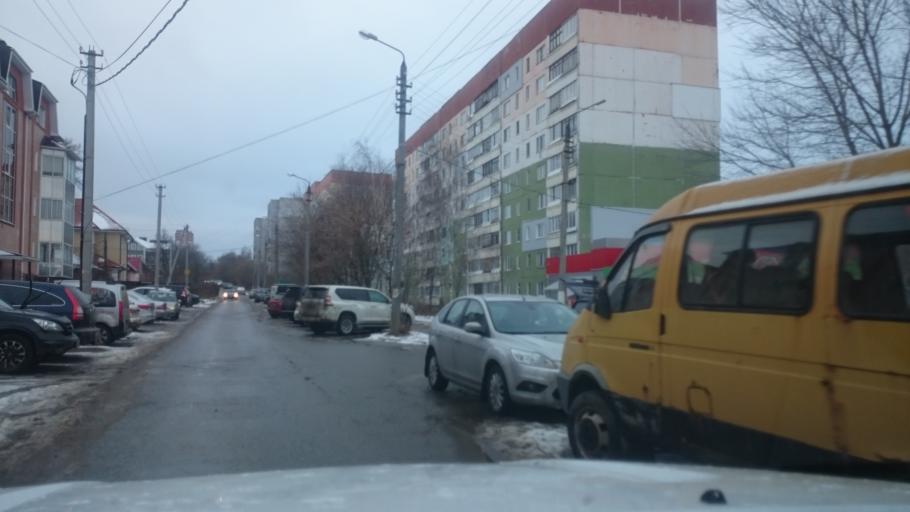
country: RU
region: Tula
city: Tula
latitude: 54.1849
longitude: 37.5684
